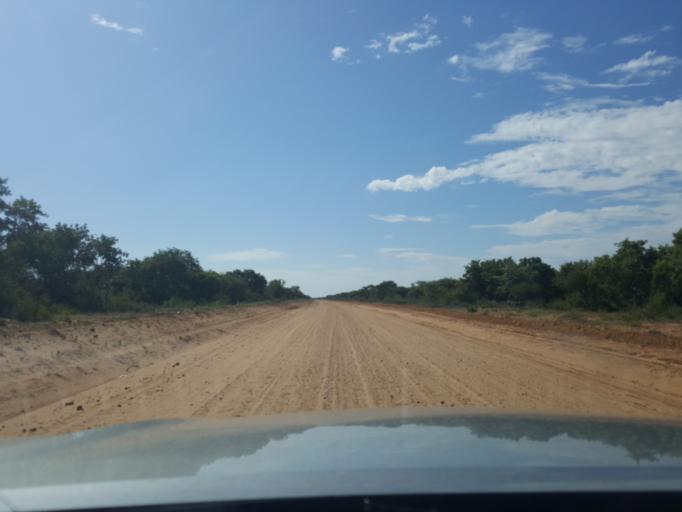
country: BW
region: Kweneng
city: Khudumelapye
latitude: -23.7239
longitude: 24.7396
